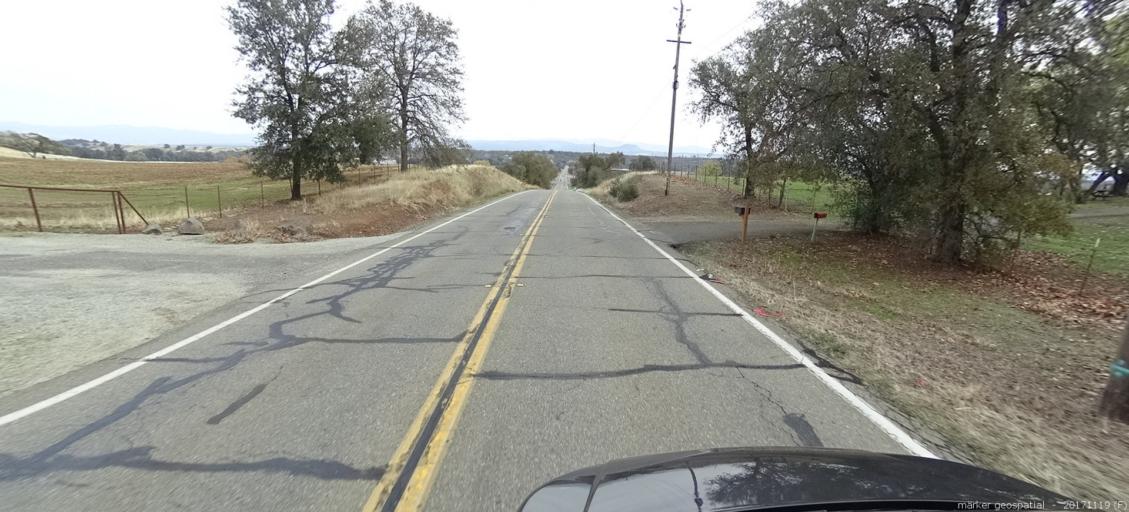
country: US
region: California
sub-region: Shasta County
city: Anderson
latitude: 40.4765
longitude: -122.2468
